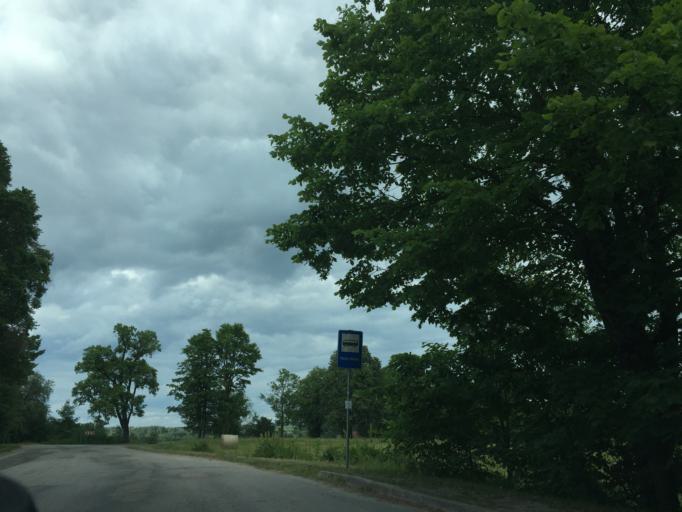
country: LV
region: Skriveri
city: Skriveri
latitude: 56.8354
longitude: 25.1321
